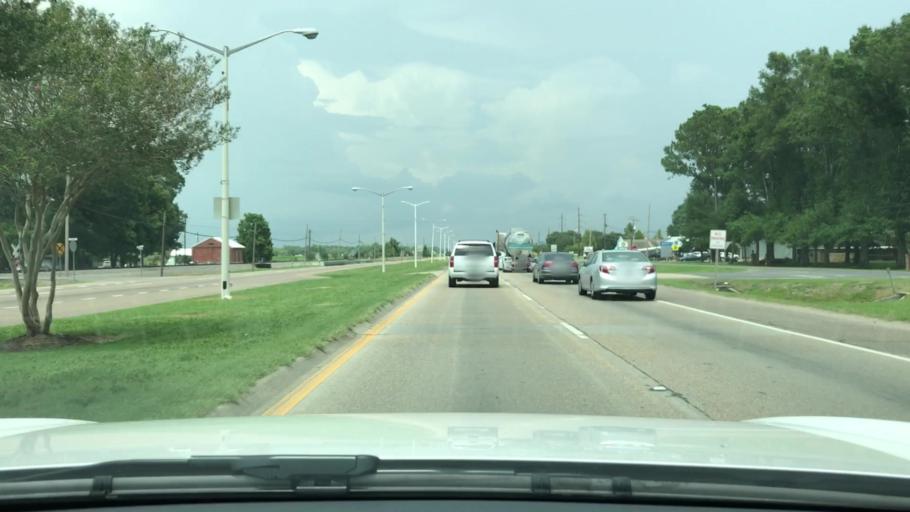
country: US
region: Louisiana
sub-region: West Baton Rouge Parish
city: Brusly
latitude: 30.3906
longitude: -91.2420
